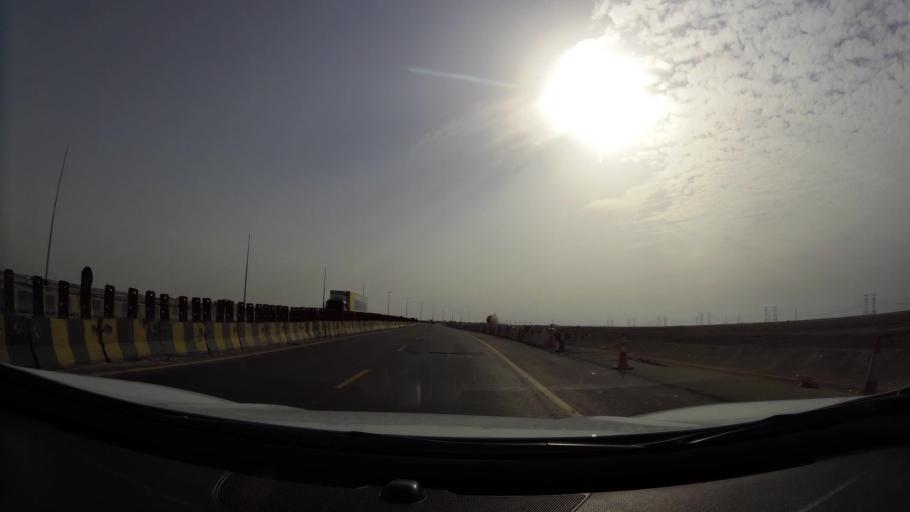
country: AE
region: Abu Dhabi
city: Abu Dhabi
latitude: 24.2372
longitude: 54.4621
